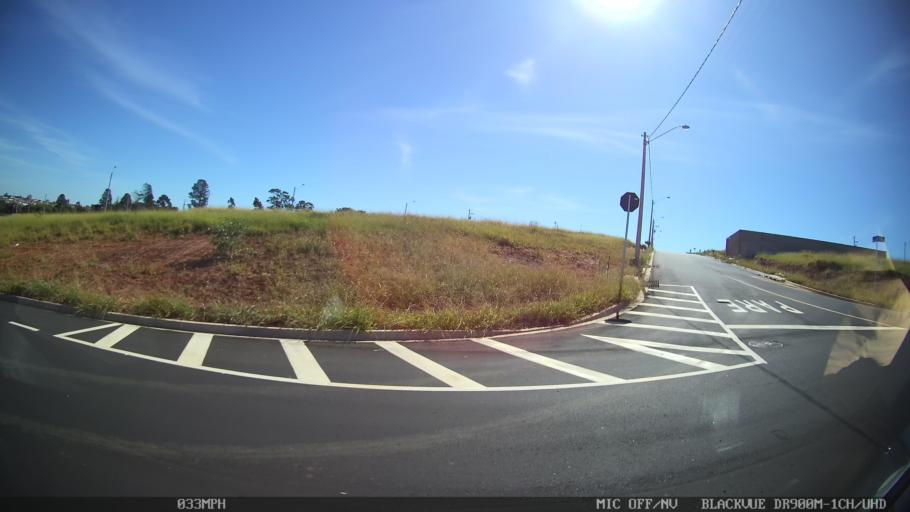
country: BR
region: Sao Paulo
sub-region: Franca
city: Franca
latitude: -20.5557
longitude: -47.3668
